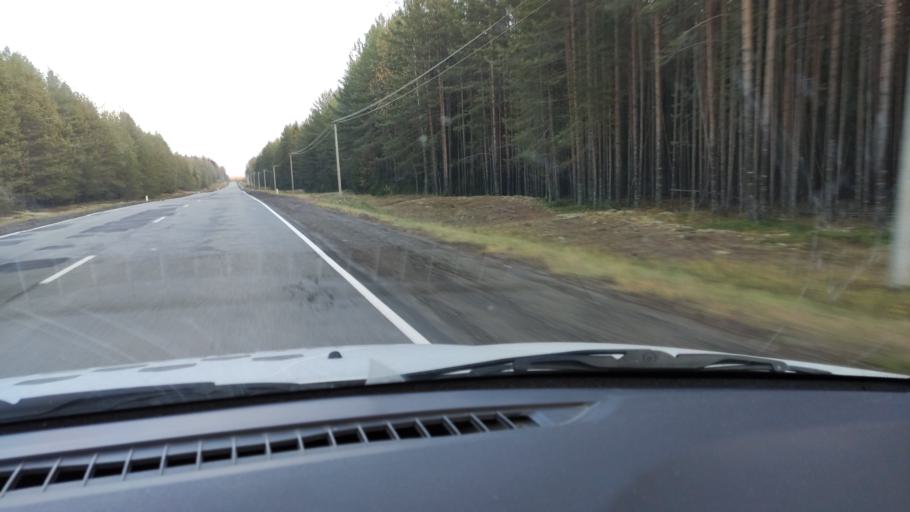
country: RU
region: Kirov
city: Belaya Kholunitsa
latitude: 58.9071
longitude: 51.0099
